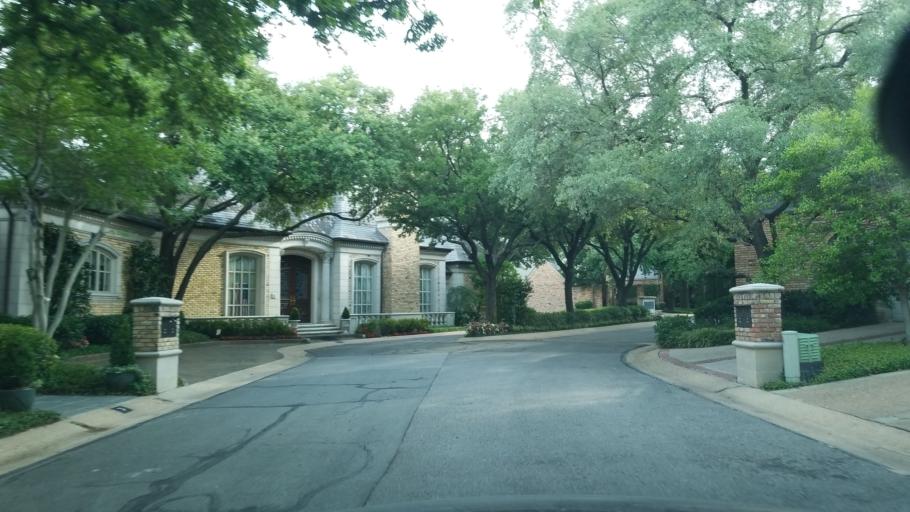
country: US
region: Texas
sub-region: Dallas County
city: University Park
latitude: 32.8600
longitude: -96.7735
